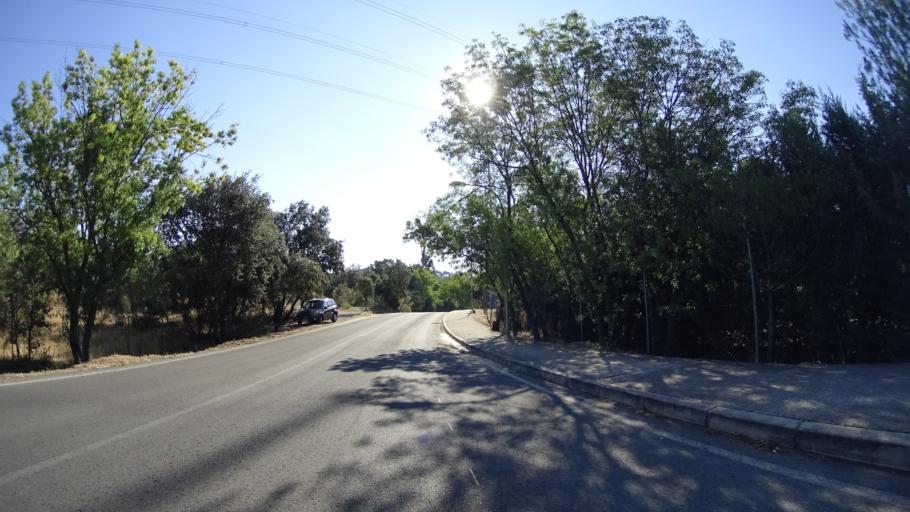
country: ES
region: Madrid
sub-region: Provincia de Madrid
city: Las Matas
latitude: 40.5829
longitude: -3.8969
